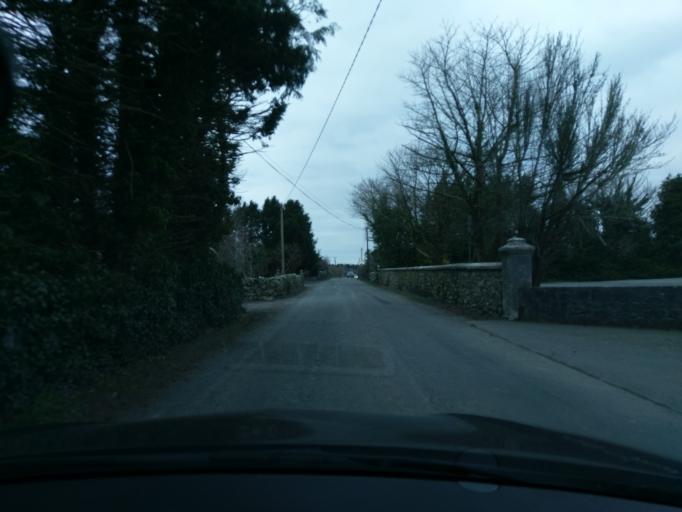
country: IE
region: Connaught
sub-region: County Galway
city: Oranmore
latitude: 53.2230
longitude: -8.8400
